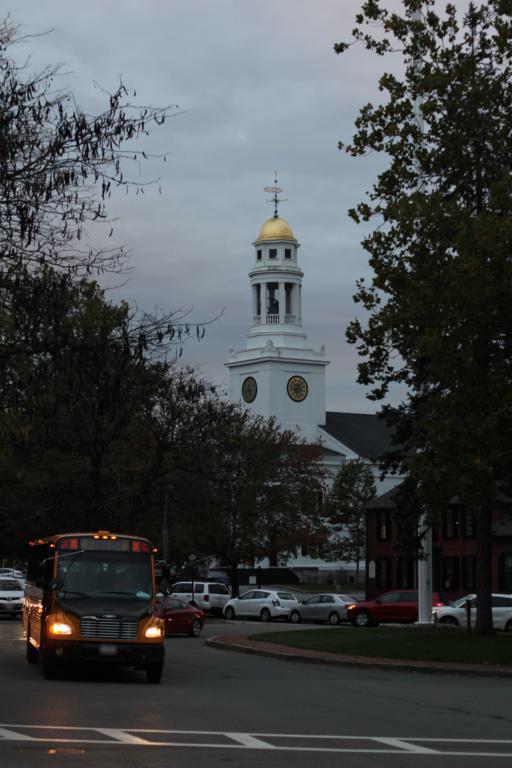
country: US
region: Massachusetts
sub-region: Middlesex County
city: Concord
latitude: 42.4597
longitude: -71.3484
